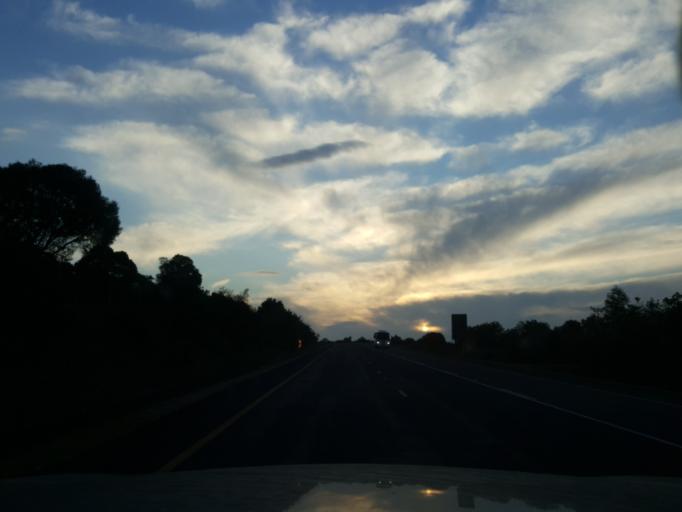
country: ZA
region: Eastern Cape
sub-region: Cacadu District Municipality
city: Grahamstown
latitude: -33.3793
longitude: 26.4587
